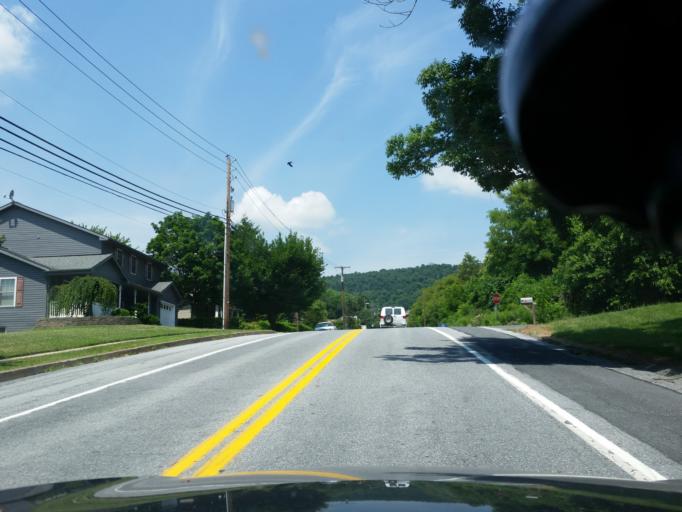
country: US
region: Pennsylvania
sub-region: Cumberland County
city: Enola
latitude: 40.3090
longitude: -76.9253
